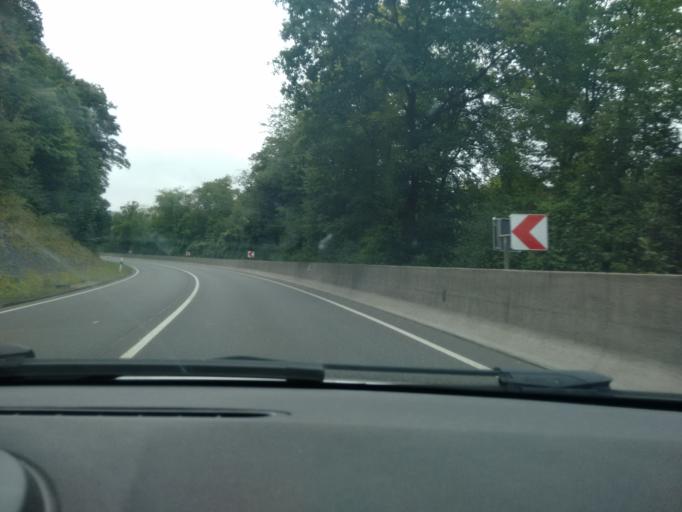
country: DE
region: Rheinland-Pfalz
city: Kirn
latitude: 49.7857
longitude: 7.4697
